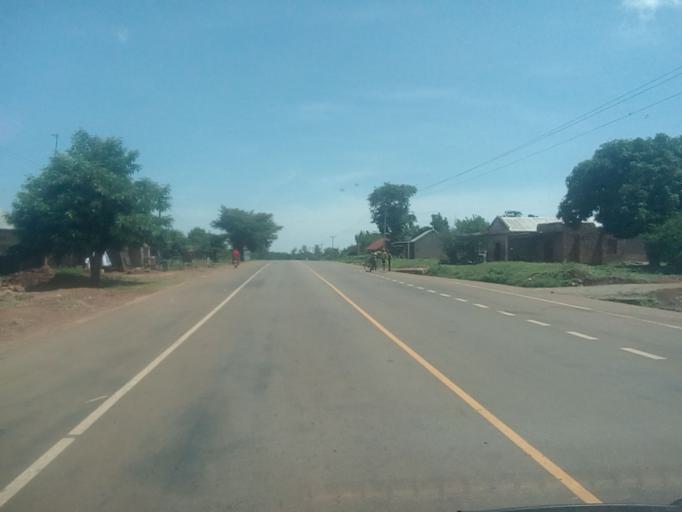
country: UG
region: Eastern Region
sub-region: Kamuli District
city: Kamuli
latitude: 0.8500
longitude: 33.1288
